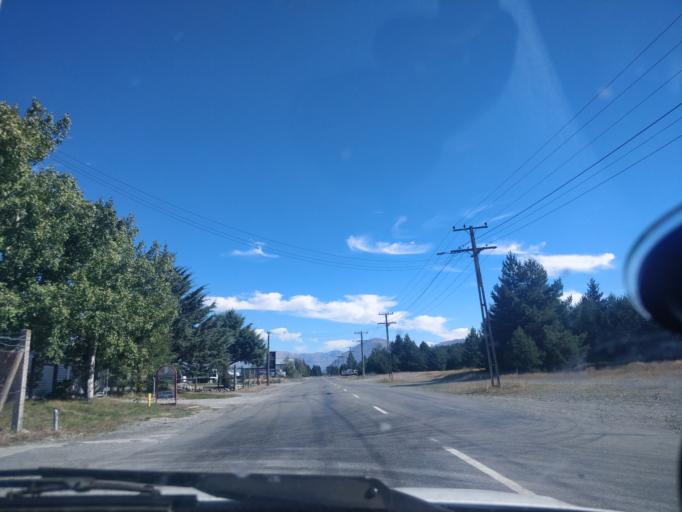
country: NZ
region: Otago
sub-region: Queenstown-Lakes District
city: Wanaka
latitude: -44.2645
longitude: 170.0909
